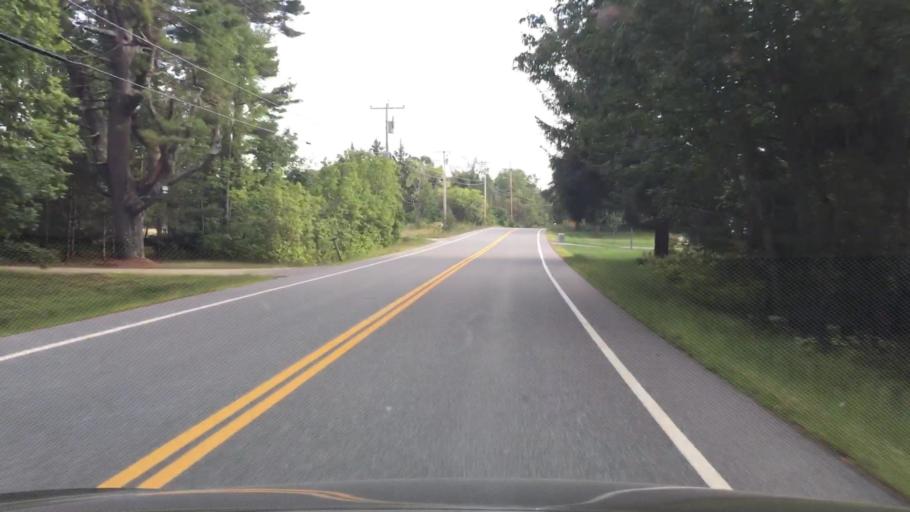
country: US
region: Maine
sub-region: Hancock County
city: Castine
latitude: 44.4438
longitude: -68.7869
